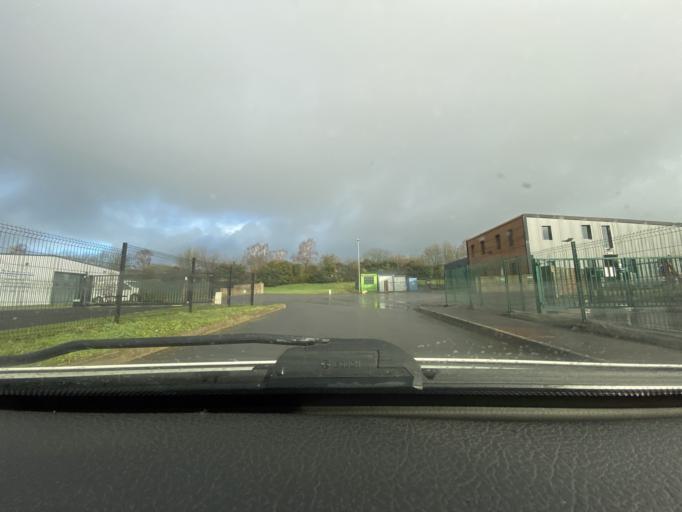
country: FR
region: Brittany
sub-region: Departement d'Ille-et-Vilaine
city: Melesse
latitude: 48.2247
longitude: -1.7062
